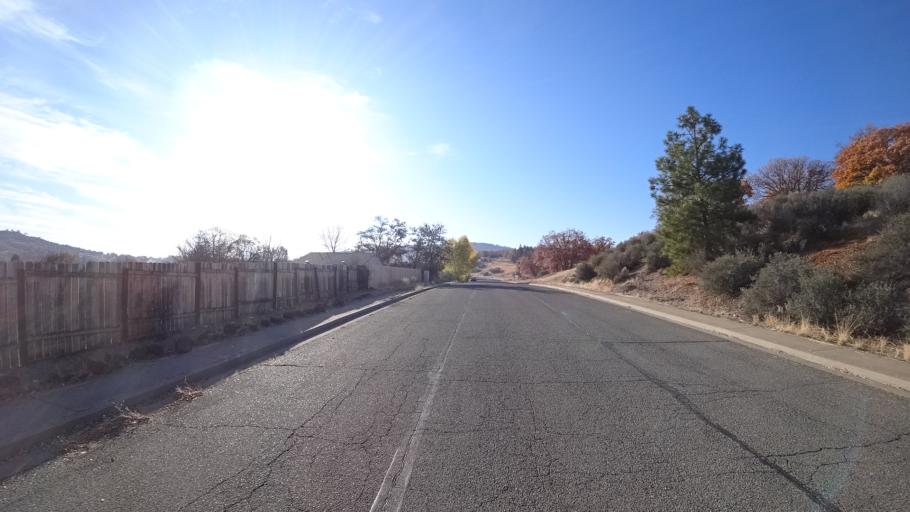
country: US
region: California
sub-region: Siskiyou County
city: Yreka
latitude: 41.7098
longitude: -122.6239
